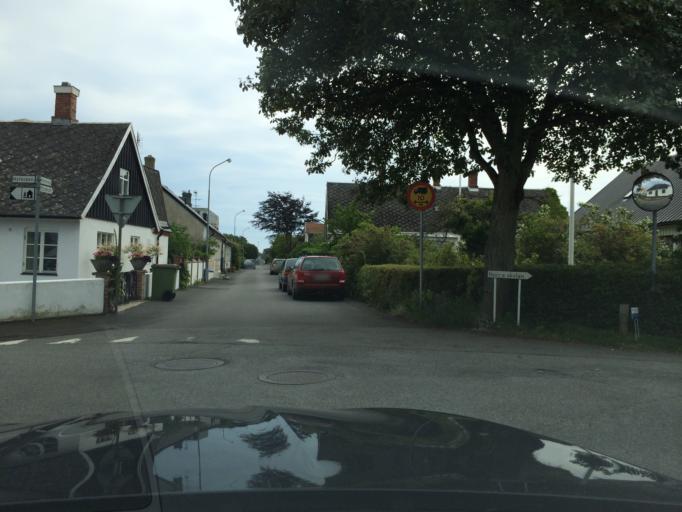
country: SE
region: Skane
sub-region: Simrishamns Kommun
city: Simrishamn
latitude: 55.5178
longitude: 14.3452
